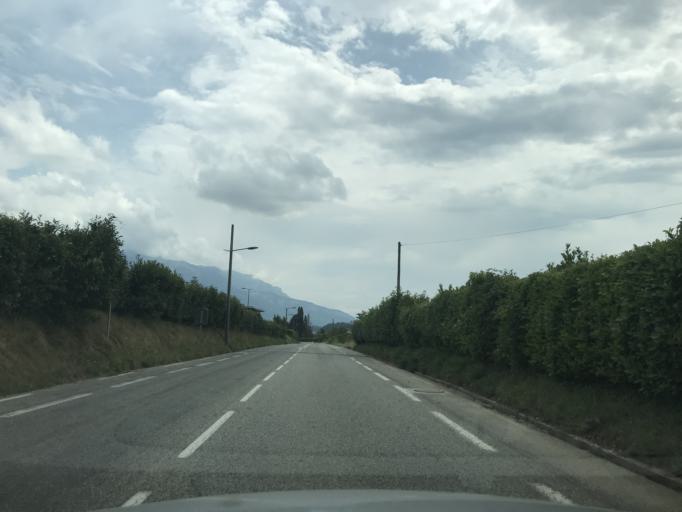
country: FR
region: Rhone-Alpes
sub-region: Departement de la Savoie
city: Brison-Saint-Innocent
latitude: 45.7182
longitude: 5.8866
